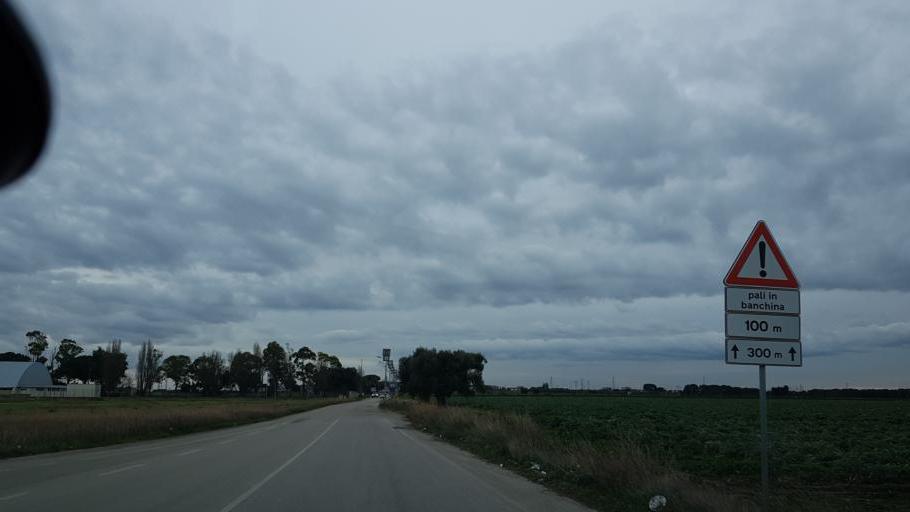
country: IT
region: Apulia
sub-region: Provincia di Brindisi
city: La Rosa
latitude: 40.6164
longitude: 17.9449
